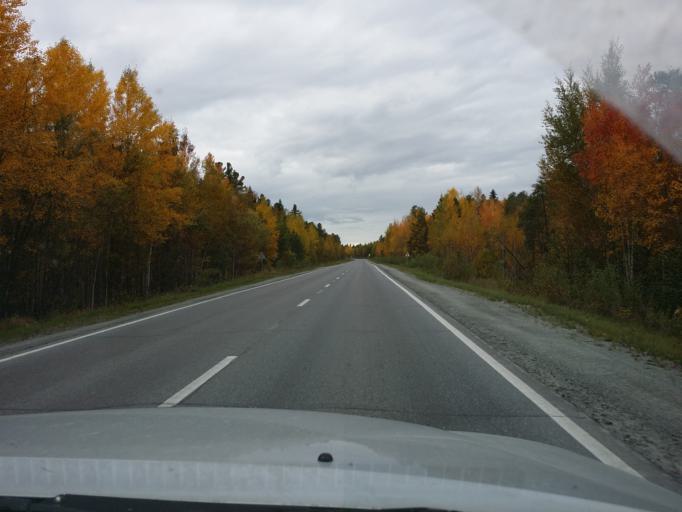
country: RU
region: Khanty-Mansiyskiy Avtonomnyy Okrug
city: Langepas
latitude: 61.2119
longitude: 75.3663
